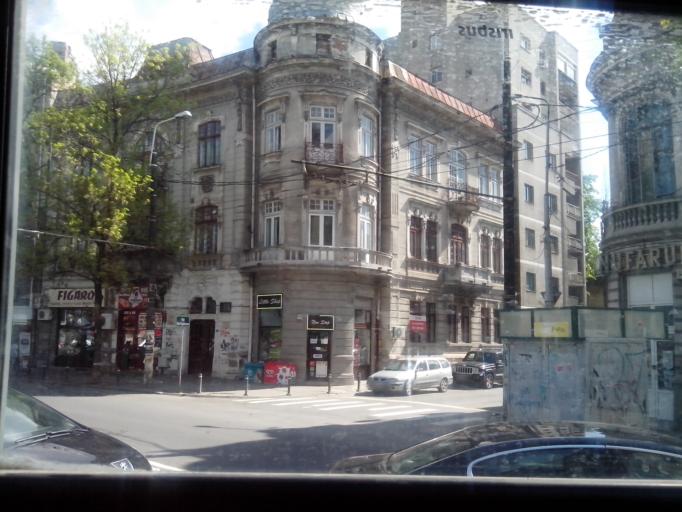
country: RO
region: Bucuresti
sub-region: Municipiul Bucuresti
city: Bucuresti
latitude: 44.4347
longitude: 26.0876
